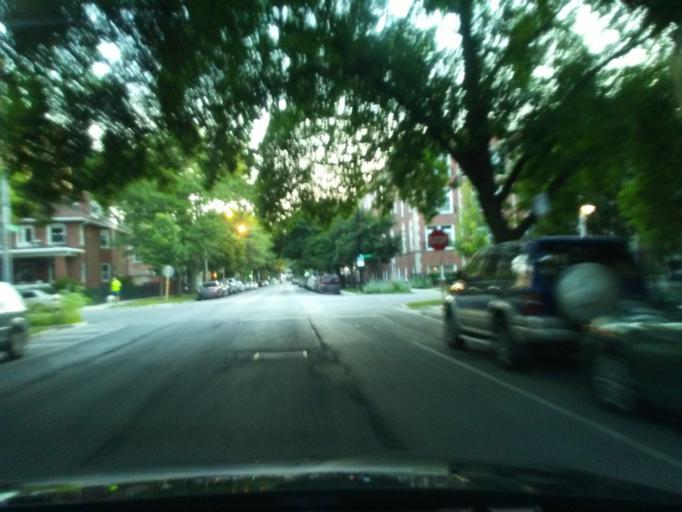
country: US
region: Illinois
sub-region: Cook County
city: Evanston
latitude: 42.0147
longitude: -87.6703
